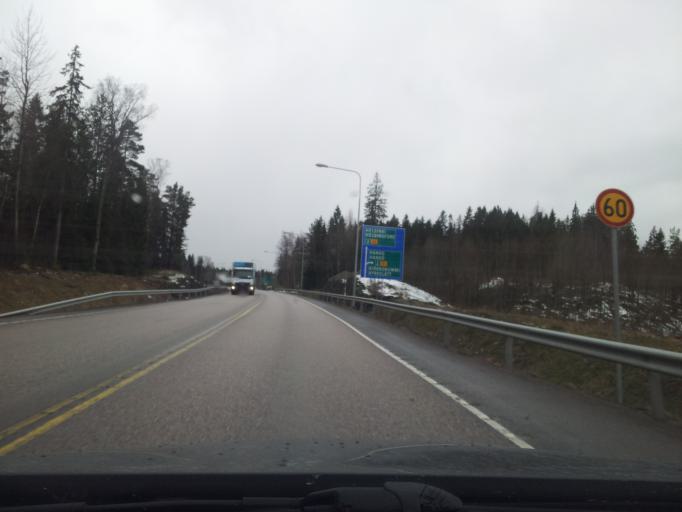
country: FI
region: Uusimaa
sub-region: Helsinki
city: Kirkkonummi
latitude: 60.1414
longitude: 24.5353
